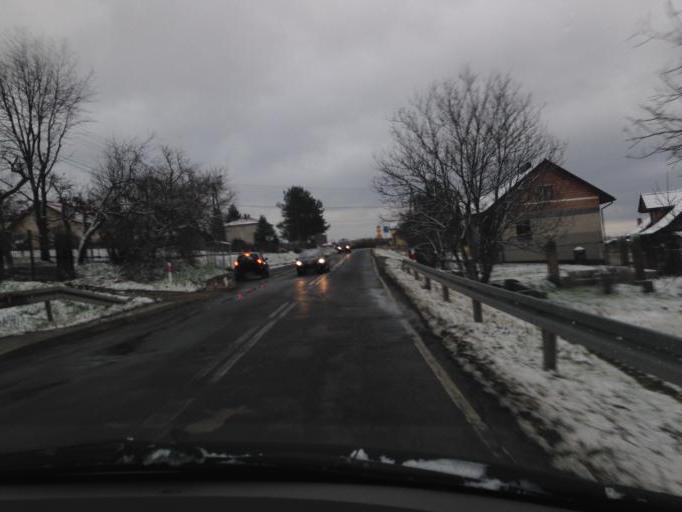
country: PL
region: Lesser Poland Voivodeship
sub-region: Powiat brzeski
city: Gnojnik
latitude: 49.8531
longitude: 20.6313
